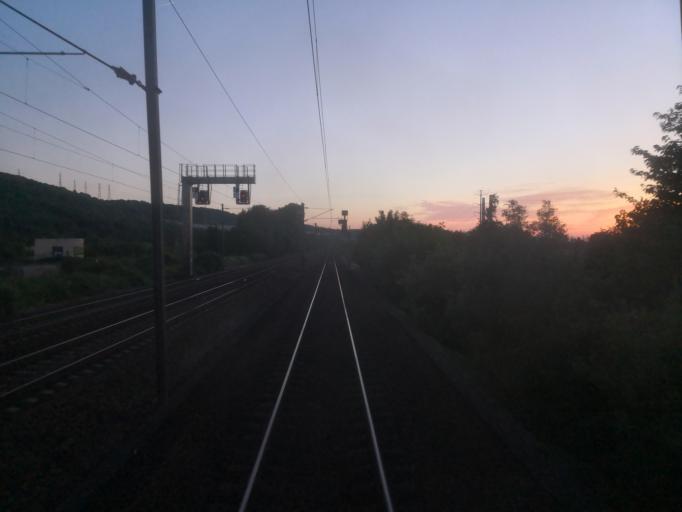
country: FR
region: Ile-de-France
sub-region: Departement des Yvelines
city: Mezieres-sur-Seine
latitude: 48.9632
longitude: 1.7909
